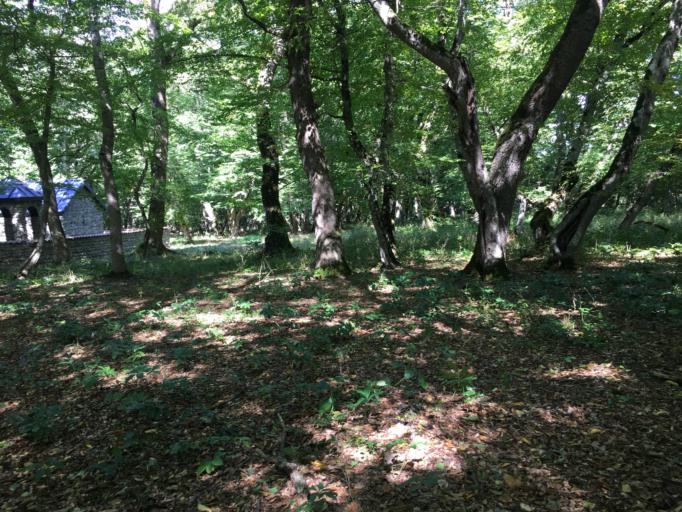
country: GE
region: Mtskheta-Mtianeti
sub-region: Tianetis Munitsip'alit'et'i
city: T'ianet'i
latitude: 41.9333
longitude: 44.9745
